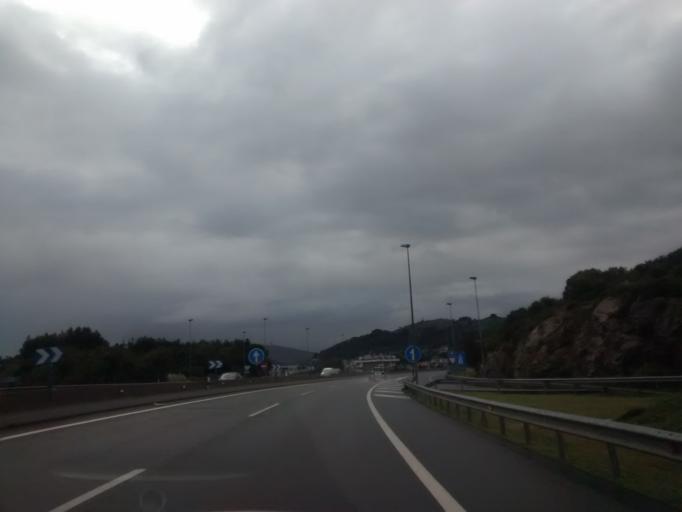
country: ES
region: Cantabria
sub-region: Provincia de Cantabria
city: Castro-Urdiales
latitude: 43.3944
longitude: -3.2358
